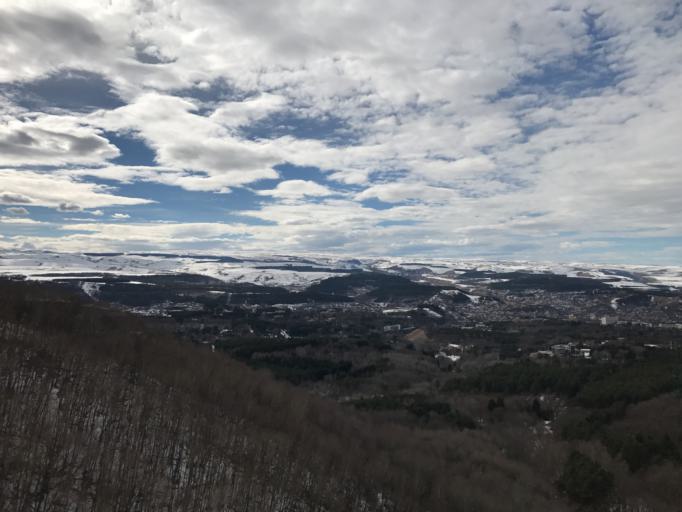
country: RU
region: Stavropol'skiy
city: Kislovodsk
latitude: 43.8984
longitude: 42.7563
